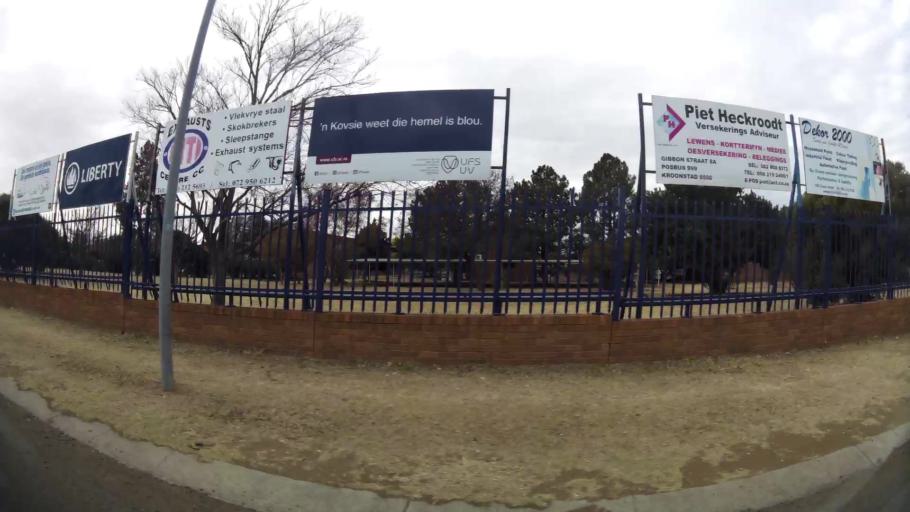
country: ZA
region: Orange Free State
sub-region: Fezile Dabi District Municipality
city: Kroonstad
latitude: -27.6359
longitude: 27.2338
